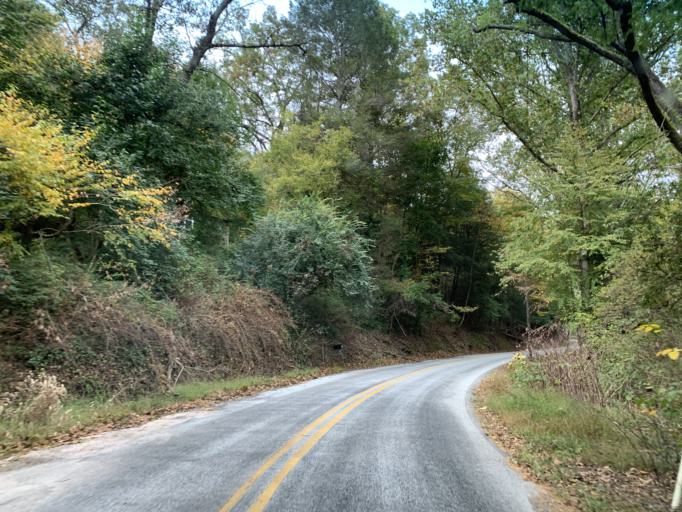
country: US
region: Pennsylvania
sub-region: York County
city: Susquehanna Trails
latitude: 39.7885
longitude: -76.4165
